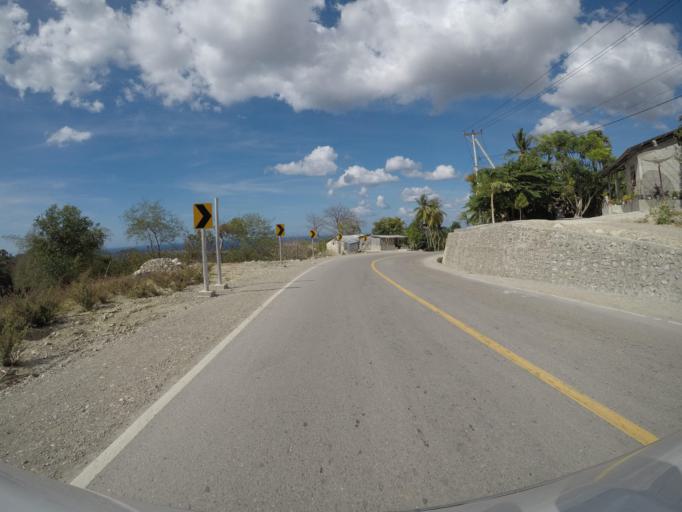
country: TL
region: Baucau
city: Baucau
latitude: -8.4698
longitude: 126.4867
